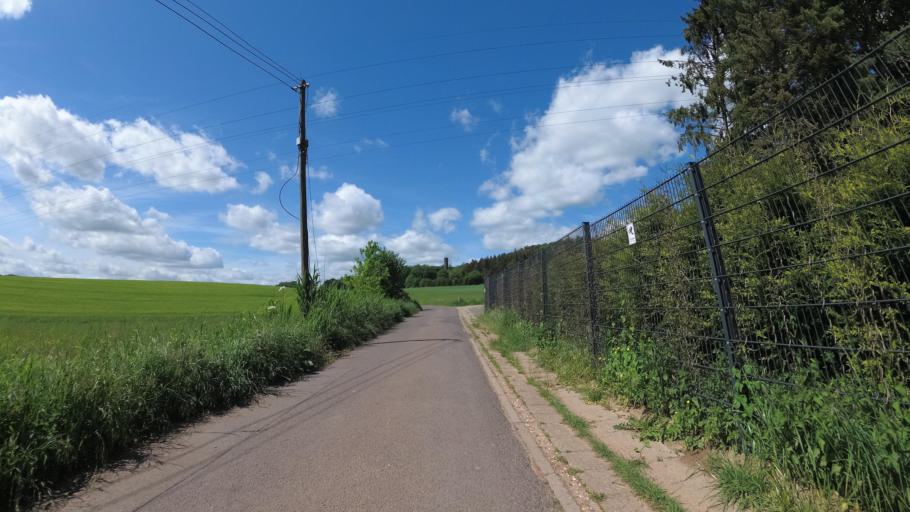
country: DE
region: Saarland
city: Lebach
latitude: 49.4207
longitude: 6.8967
